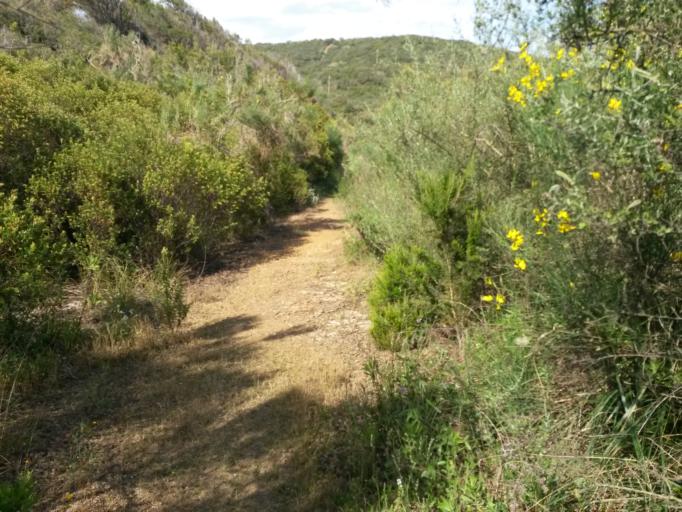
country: IT
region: Tuscany
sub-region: Provincia di Livorno
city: Porto Azzurro
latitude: 42.7732
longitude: 10.4183
